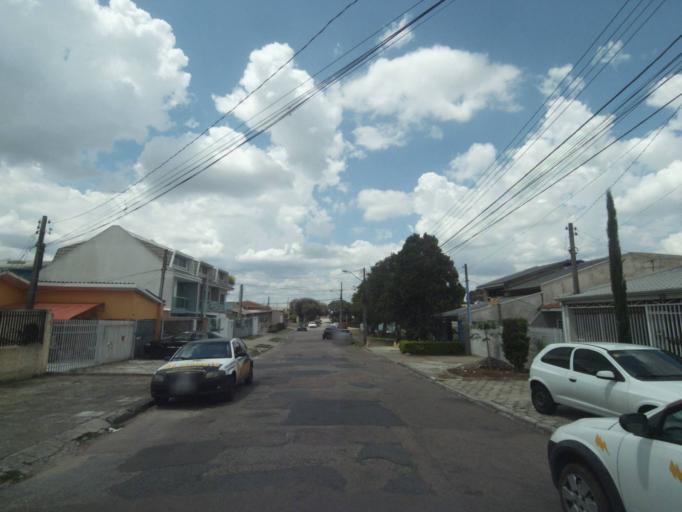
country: BR
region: Parana
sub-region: Sao Jose Dos Pinhais
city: Sao Jose dos Pinhais
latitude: -25.5403
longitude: -49.2709
